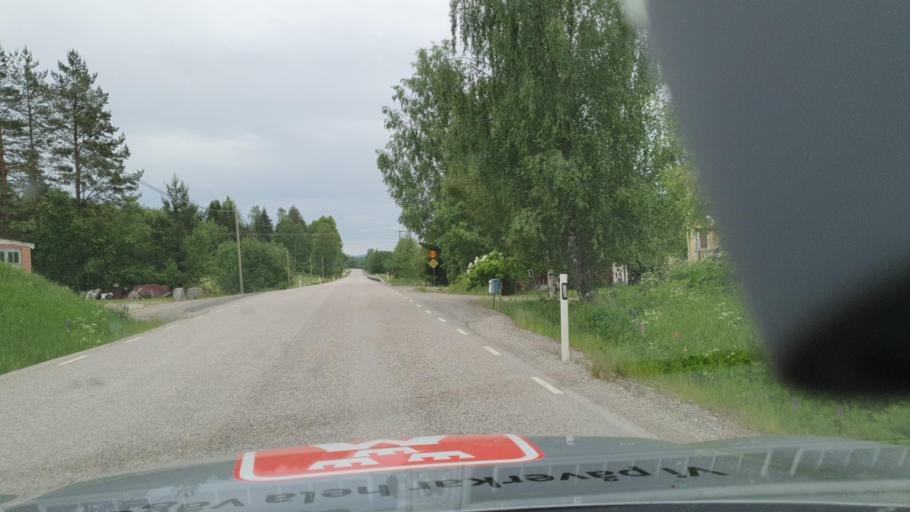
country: SE
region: Vaesternorrland
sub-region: Kramfors Kommun
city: Kramfors
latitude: 62.9400
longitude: 17.9053
